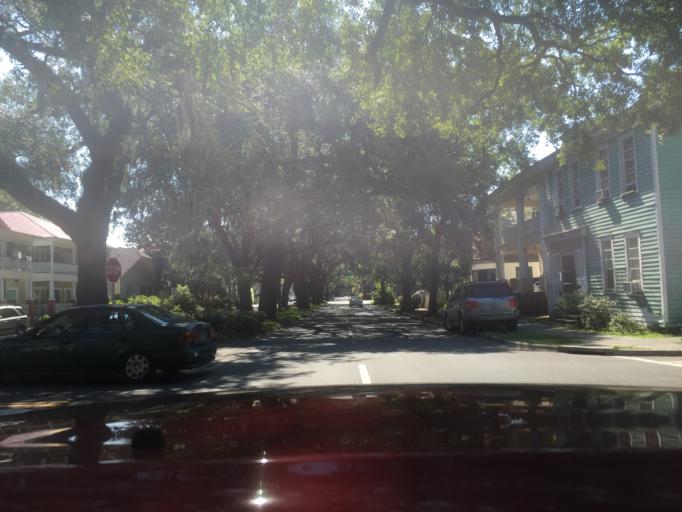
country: US
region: Georgia
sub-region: Chatham County
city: Savannah
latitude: 32.0589
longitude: -81.1069
